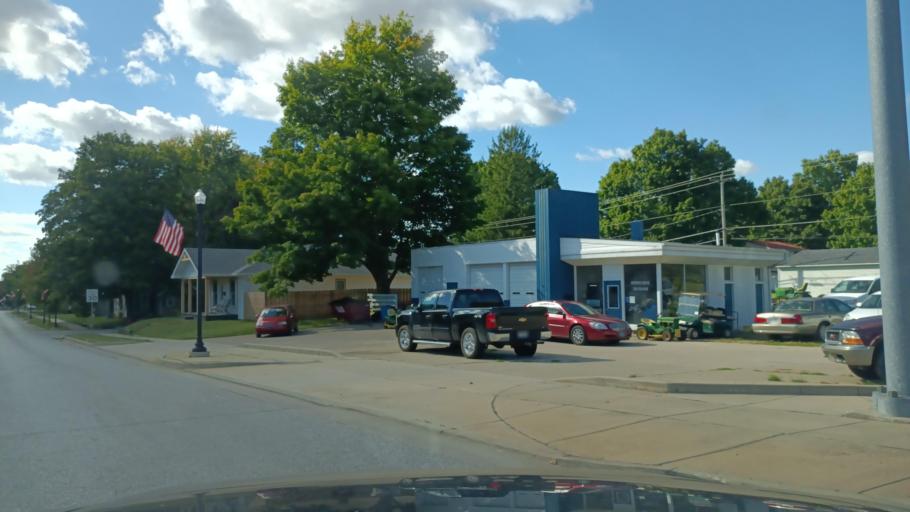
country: US
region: Indiana
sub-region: Fountain County
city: Covington
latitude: 40.1382
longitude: -87.3870
